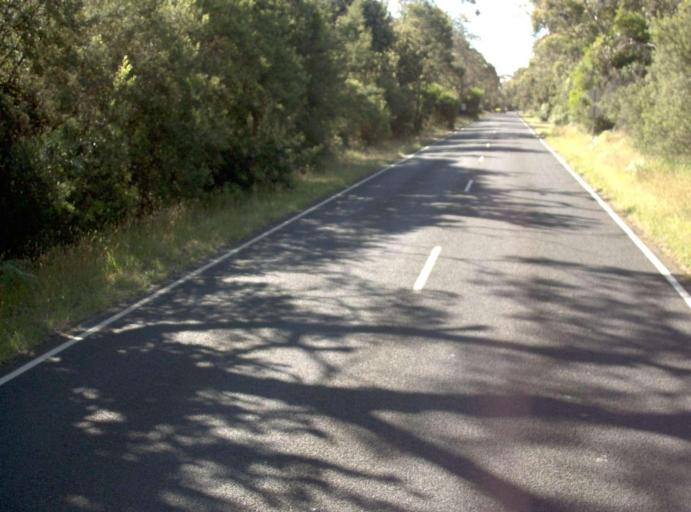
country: AU
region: Victoria
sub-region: Latrobe
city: Traralgon
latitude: -38.6569
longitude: 146.6799
